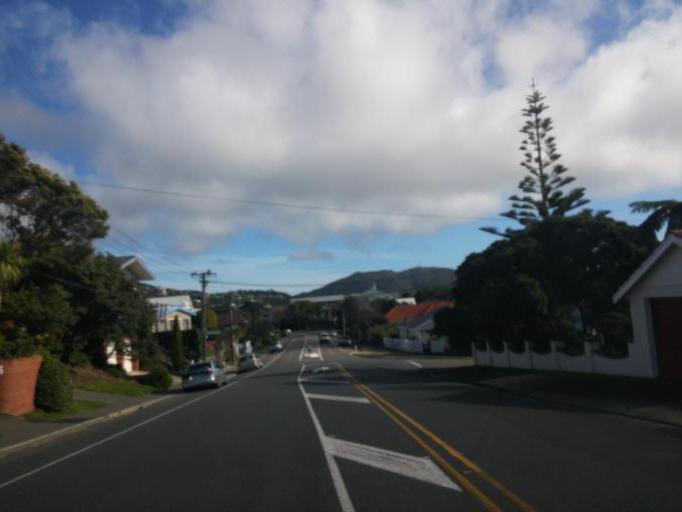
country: NZ
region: Wellington
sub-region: Wellington City
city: Kelburn
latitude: -41.2842
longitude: 174.7482
